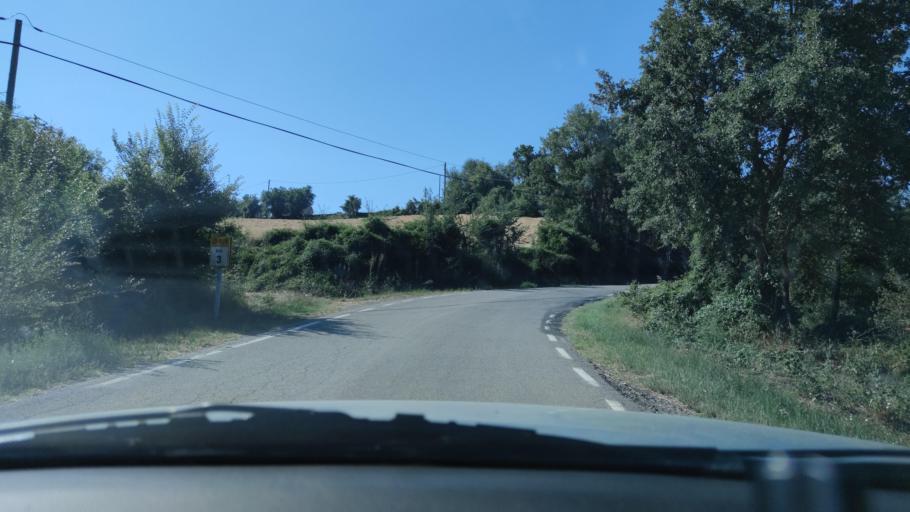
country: ES
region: Catalonia
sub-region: Provincia de Lleida
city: Sant Guim de Freixenet
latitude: 41.6797
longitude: 1.4041
